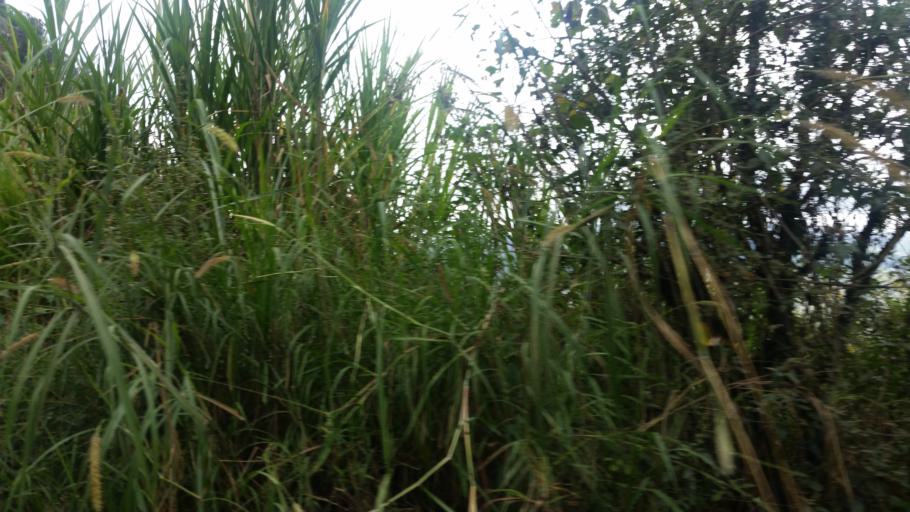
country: CO
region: Cundinamarca
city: Choachi
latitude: 4.5141
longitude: -73.9300
